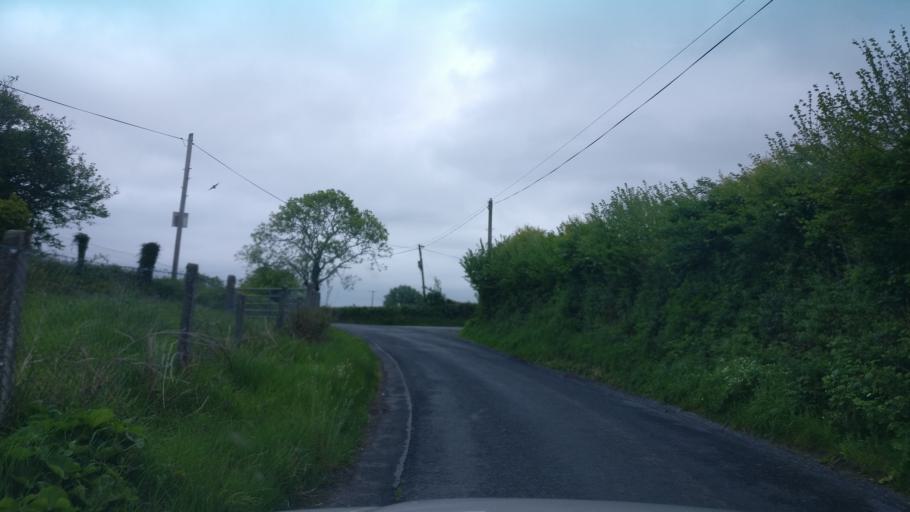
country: IE
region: Connaught
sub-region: County Galway
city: Portumna
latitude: 53.1414
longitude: -8.2890
